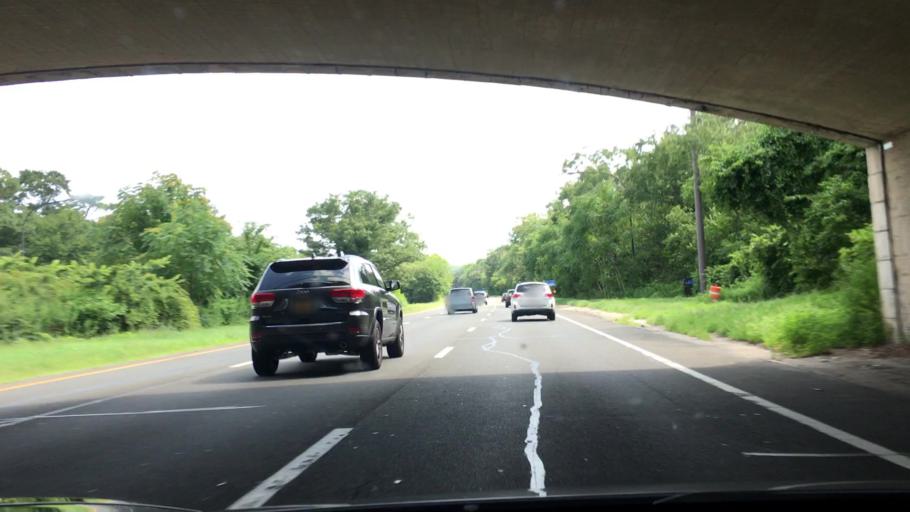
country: US
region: New York
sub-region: Nassau County
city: North Merrick
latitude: 40.6800
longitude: -73.5723
